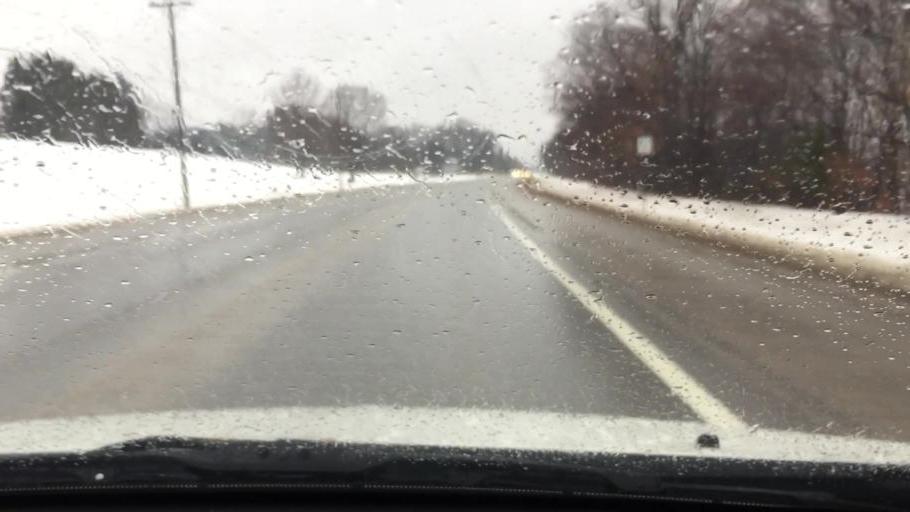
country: US
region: Michigan
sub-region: Charlevoix County
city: Charlevoix
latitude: 45.2836
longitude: -85.2399
